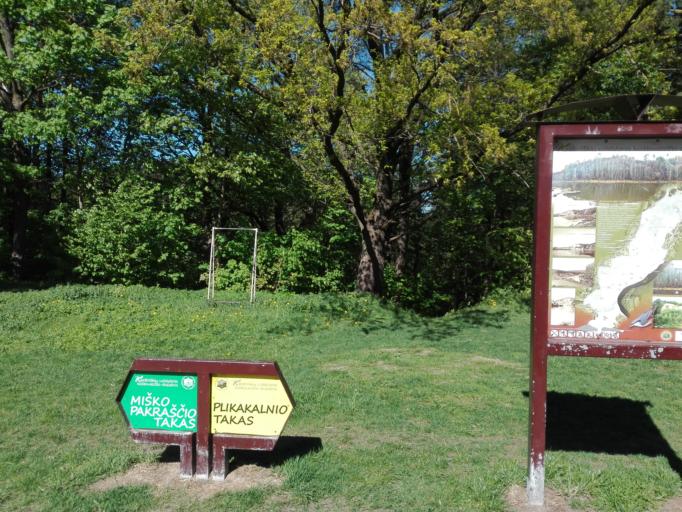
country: LT
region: Vilnius County
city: Lazdynai
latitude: 54.6842
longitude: 25.2189
